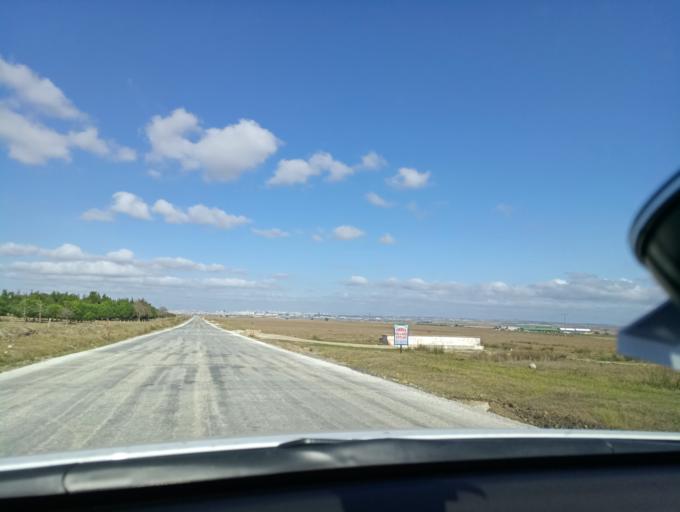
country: TR
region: Tekirdag
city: Corlu
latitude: 41.0614
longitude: 27.8343
